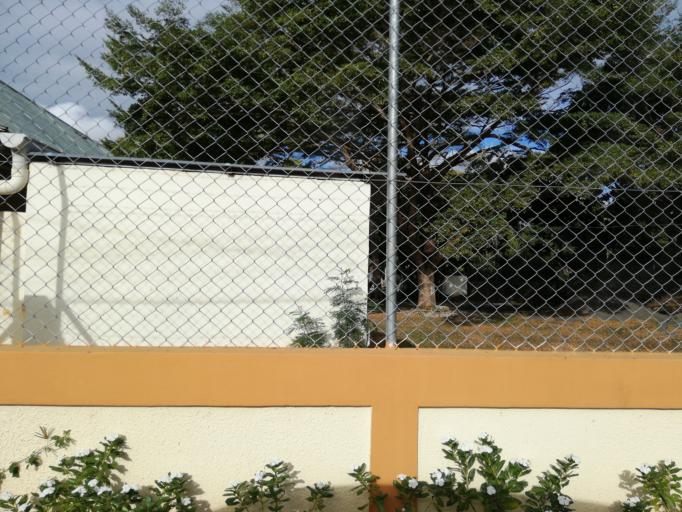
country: MU
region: Black River
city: Petite Riviere
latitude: -20.2250
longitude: 57.4591
